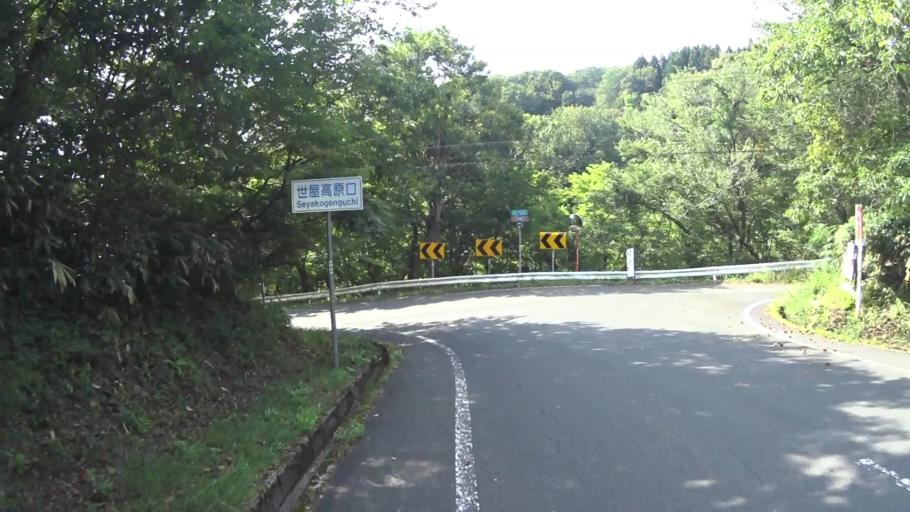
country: JP
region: Kyoto
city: Miyazu
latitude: 35.6399
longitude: 135.1839
